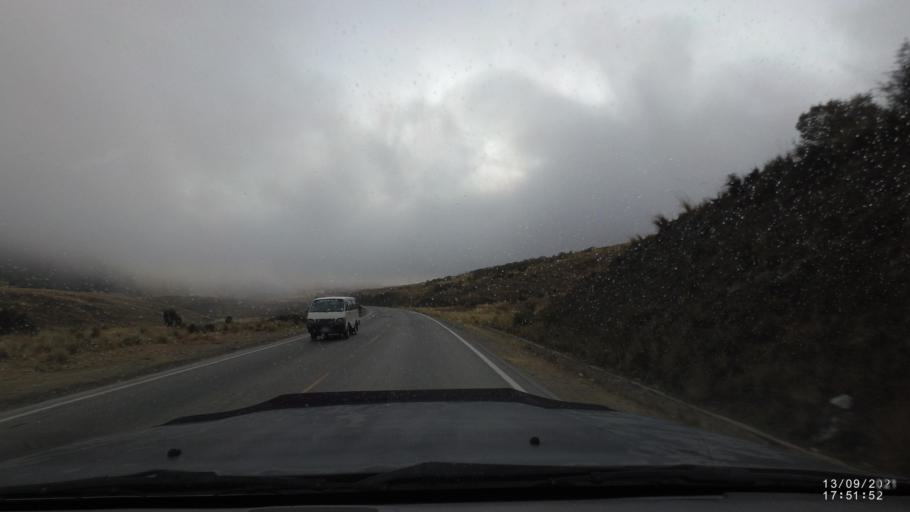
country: BO
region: Cochabamba
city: Colomi
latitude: -17.4006
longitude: -65.8754
